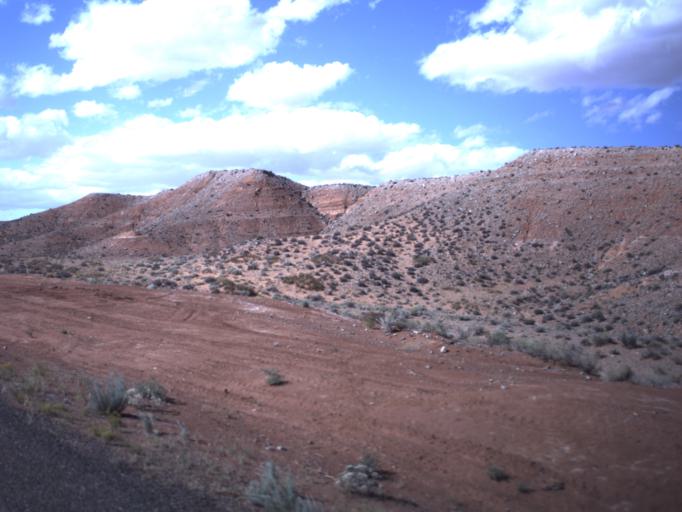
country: US
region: Utah
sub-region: Wayne County
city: Loa
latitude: 38.1447
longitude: -110.6129
